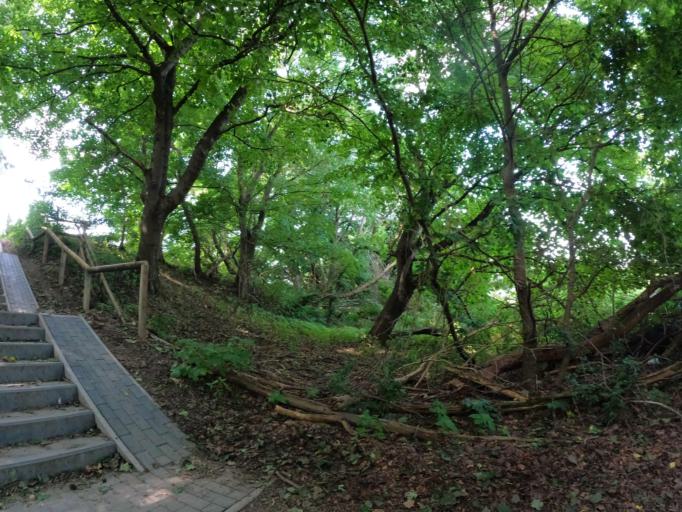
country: DE
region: Mecklenburg-Vorpommern
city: Malchow
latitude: 53.4945
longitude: 12.4372
